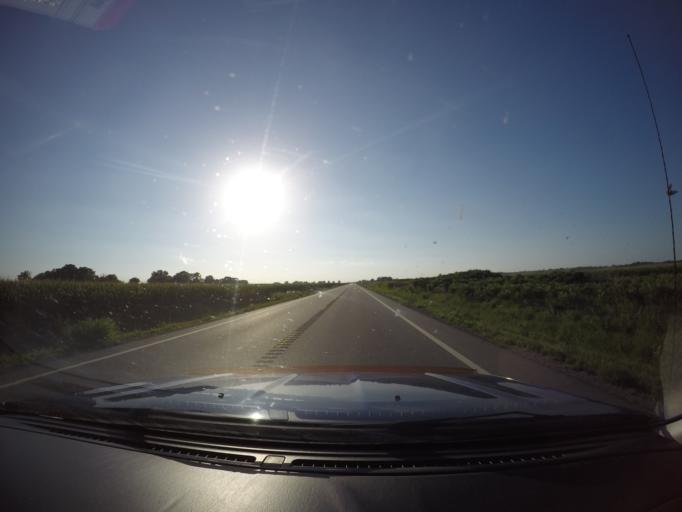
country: US
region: Kansas
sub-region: Shawnee County
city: Rossville
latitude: 39.1526
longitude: -95.9831
